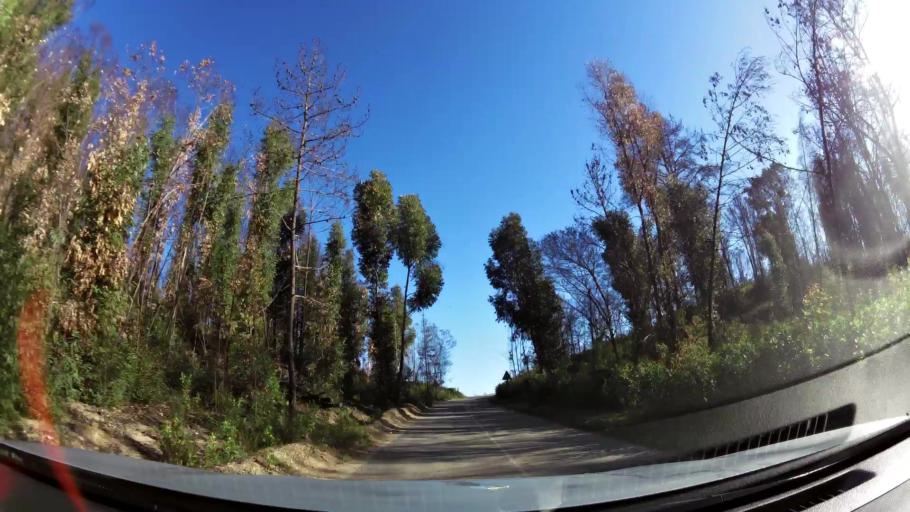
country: ZA
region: Western Cape
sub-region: Eden District Municipality
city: Knysna
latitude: -34.0246
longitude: 23.0080
